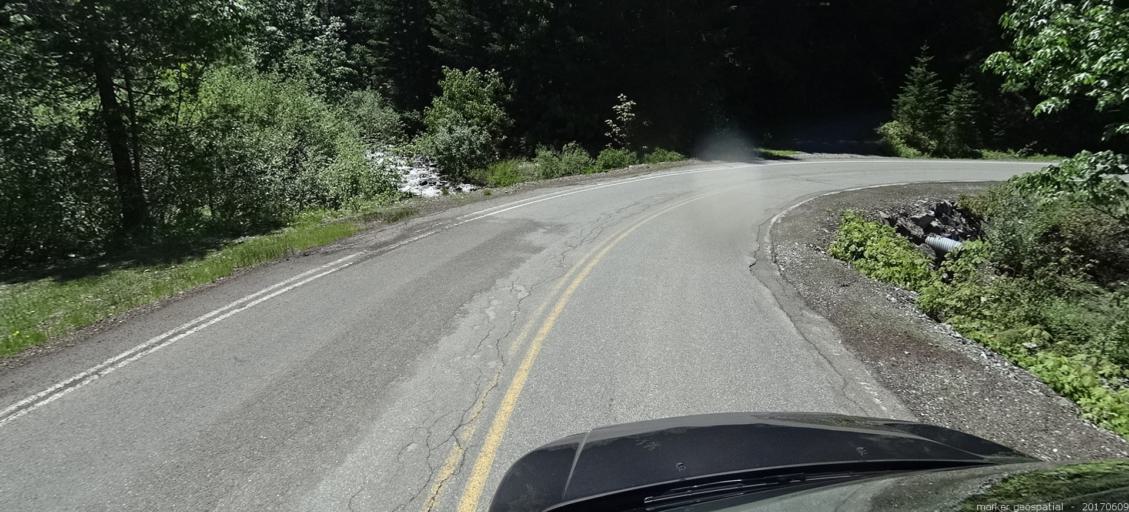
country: US
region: California
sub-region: Siskiyou County
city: Yreka
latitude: 41.4116
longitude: -122.9732
